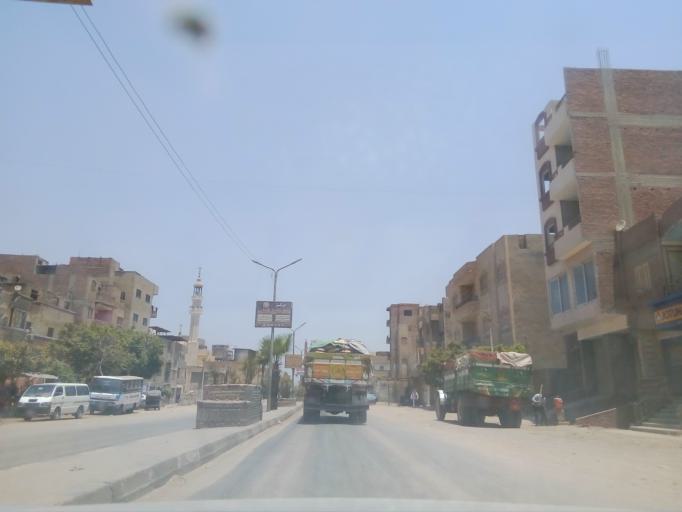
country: EG
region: Muhafazat al Qahirah
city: Halwan
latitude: 29.8490
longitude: 31.2829
